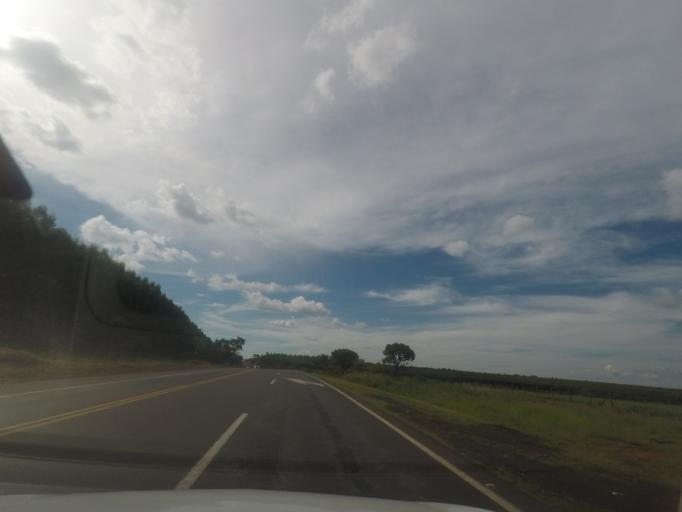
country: BR
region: Minas Gerais
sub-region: Prata
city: Prata
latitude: -19.1145
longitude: -48.9709
